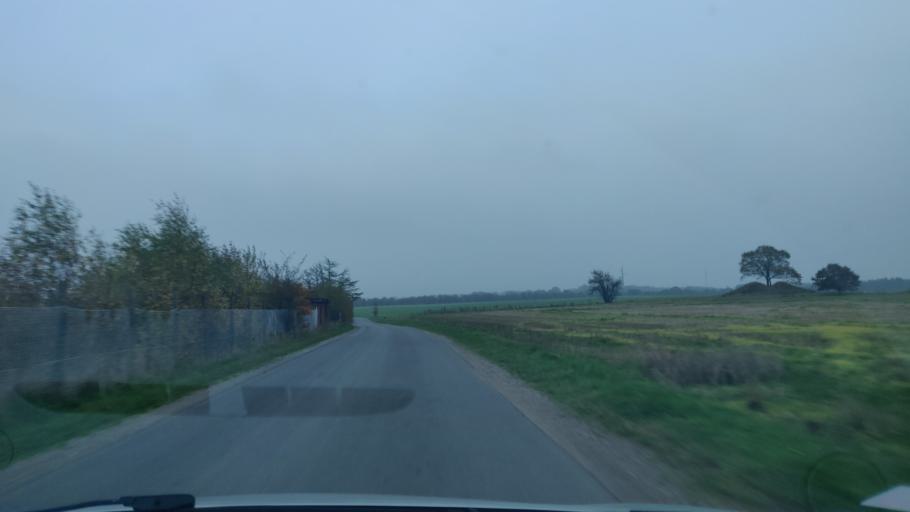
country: DK
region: South Denmark
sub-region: Kolding Kommune
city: Kolding
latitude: 55.5767
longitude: 9.4732
